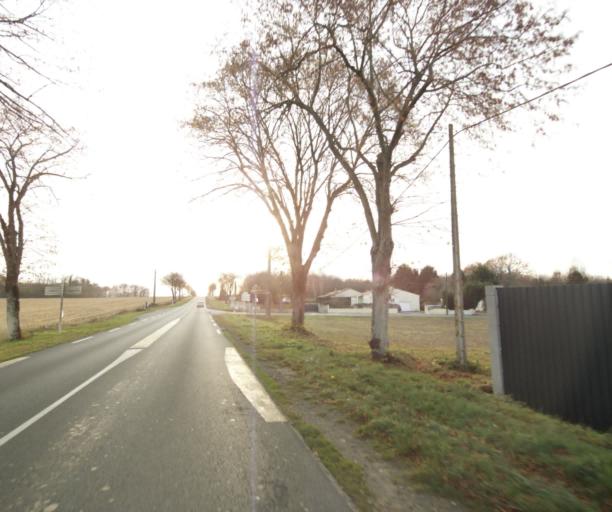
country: FR
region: Poitou-Charentes
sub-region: Departement de la Charente-Maritime
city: Saint-Hilaire-de-Villefranche
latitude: 45.8086
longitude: -0.5550
